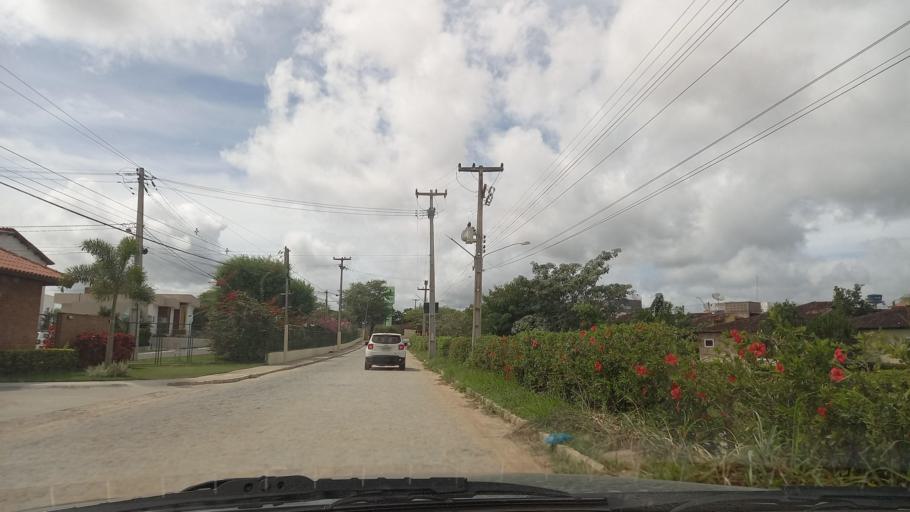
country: BR
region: Pernambuco
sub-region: Gravata
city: Gravata
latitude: -8.1938
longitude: -35.5762
